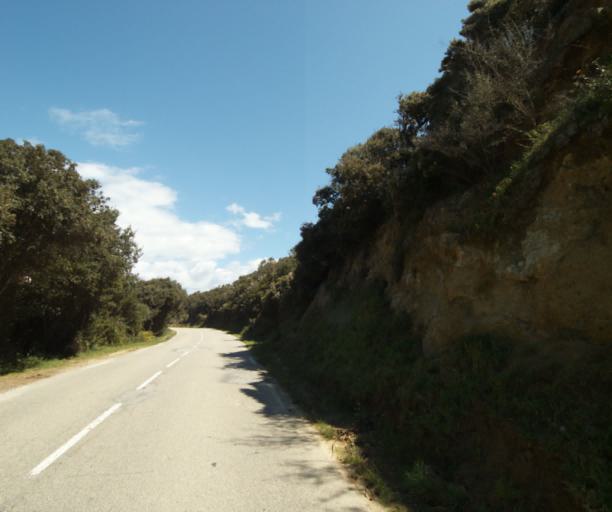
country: FR
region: Corsica
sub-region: Departement de la Corse-du-Sud
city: Propriano
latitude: 41.6477
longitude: 8.8767
